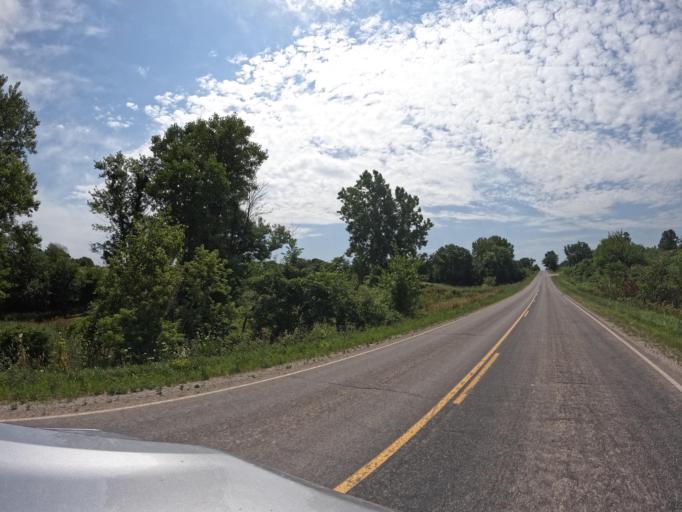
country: US
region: Iowa
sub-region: Appanoose County
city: Centerville
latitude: 40.7918
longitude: -92.9447
